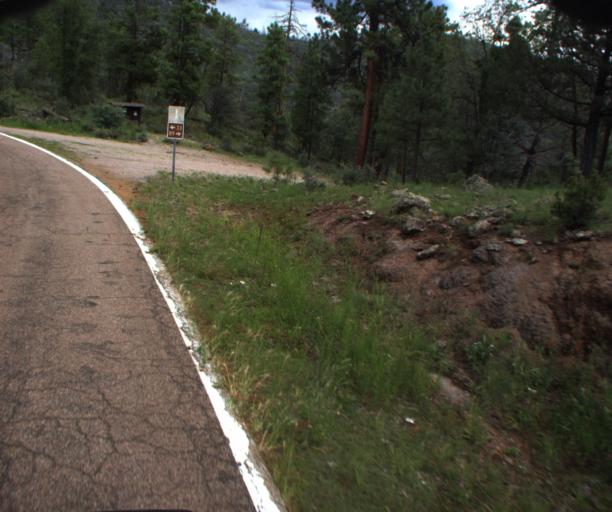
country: US
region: Arizona
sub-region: Greenlee County
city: Morenci
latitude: 33.5207
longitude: -109.3061
